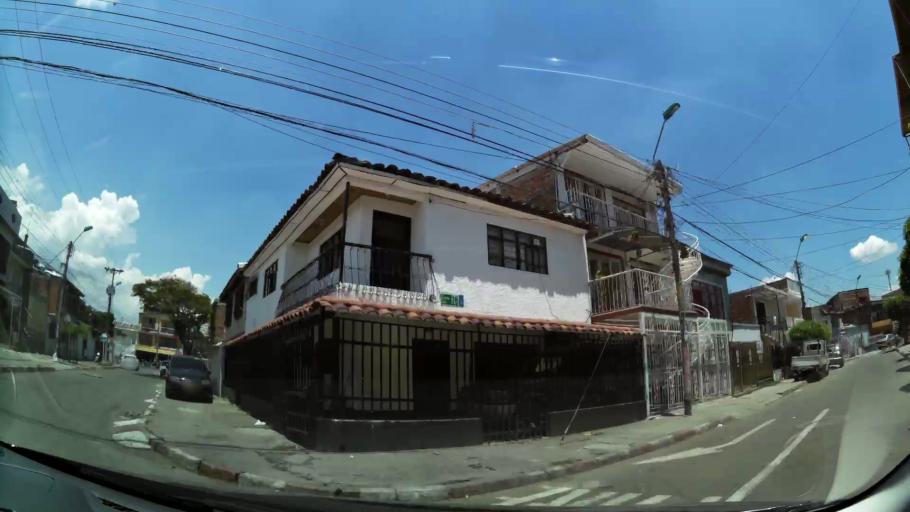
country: CO
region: Valle del Cauca
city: Cali
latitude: 3.4333
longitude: -76.5040
